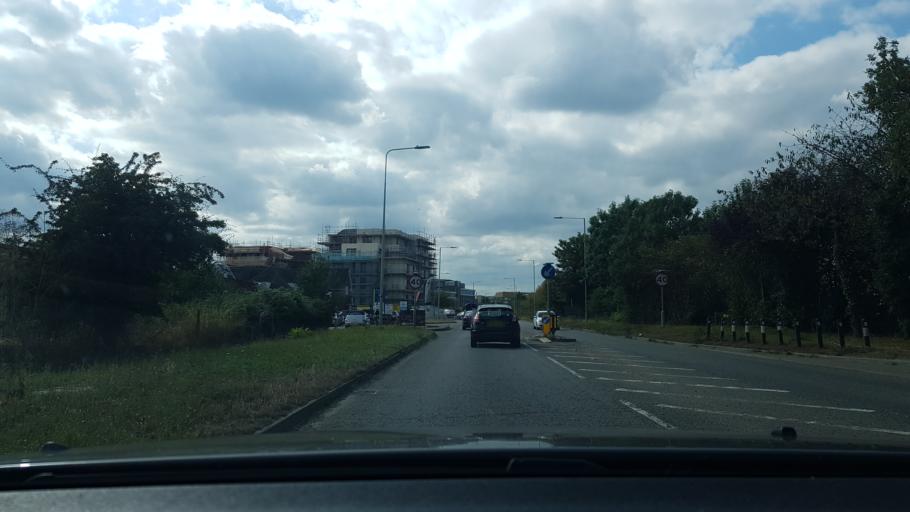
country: GB
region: England
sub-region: Surrey
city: Colnbrook
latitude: 51.4881
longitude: -0.5305
